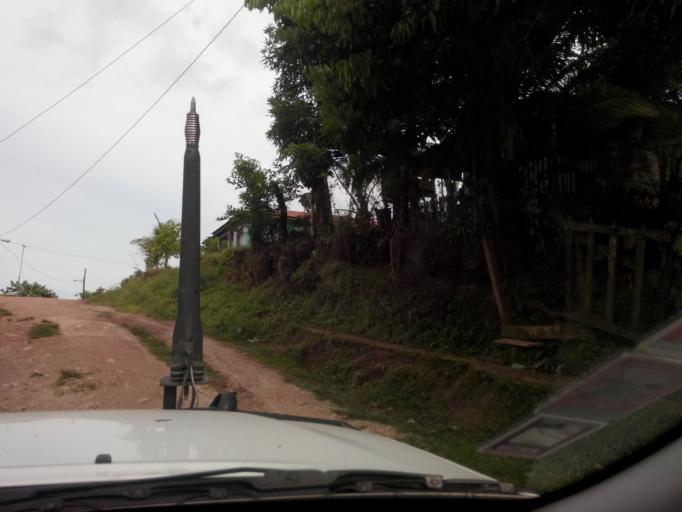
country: NI
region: Atlantico Sur
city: Bluefields
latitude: 12.0276
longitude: -83.7753
